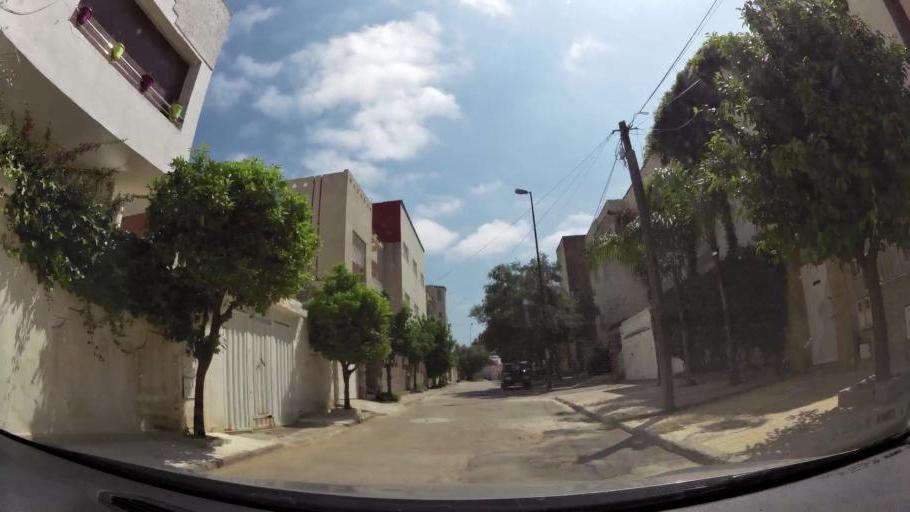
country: MA
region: Fes-Boulemane
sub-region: Fes
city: Fes
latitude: 34.0620
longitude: -5.0323
